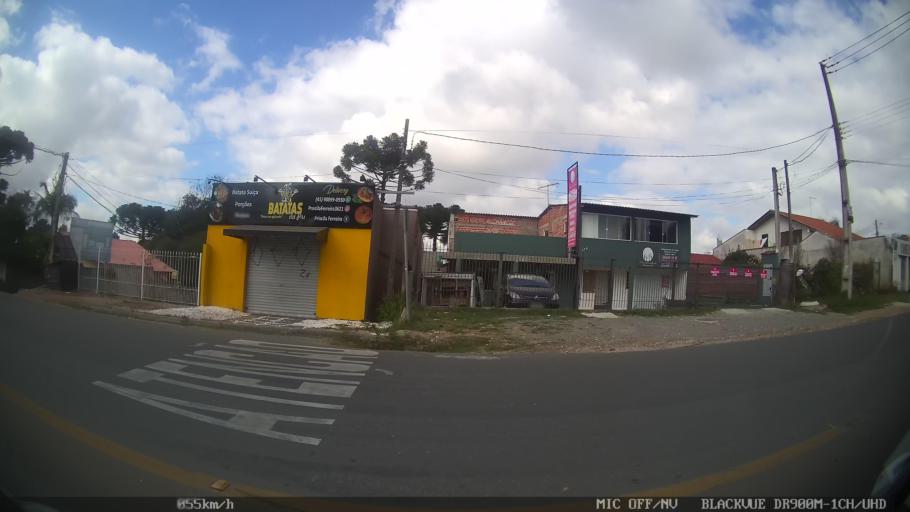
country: BR
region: Parana
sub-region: Pinhais
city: Pinhais
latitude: -25.3716
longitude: -49.2174
